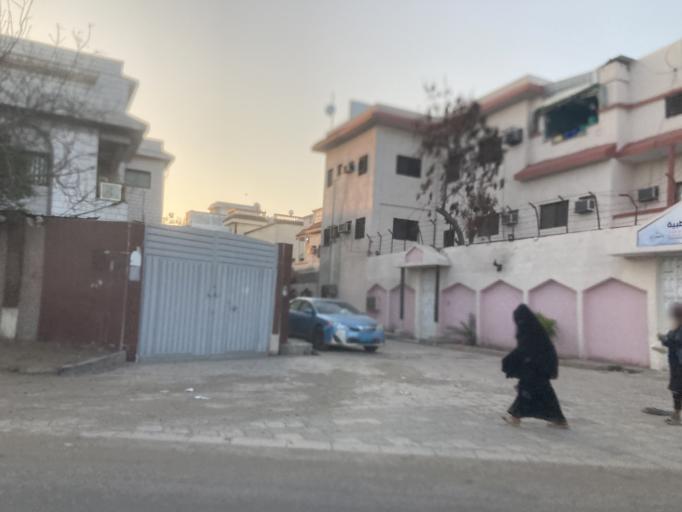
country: YE
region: Aden
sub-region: Al Mansura
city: Al Mansurah
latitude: 12.8550
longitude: 44.9919
